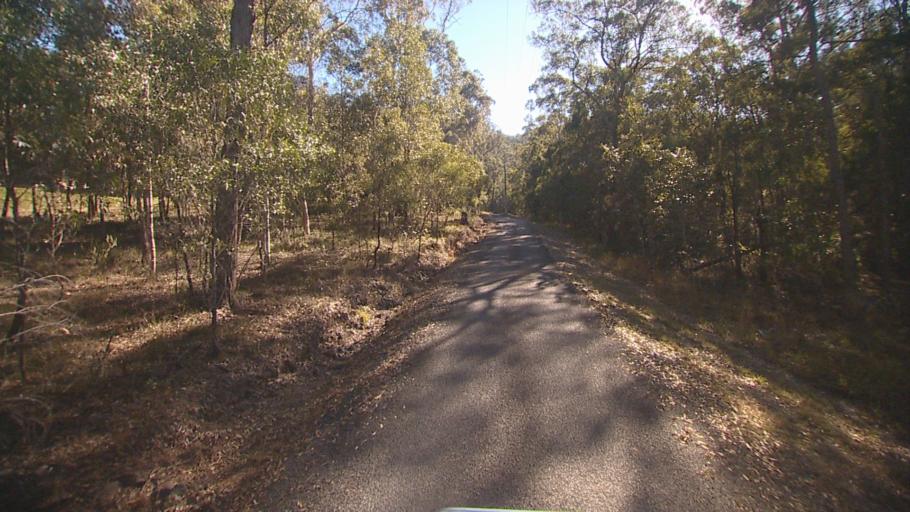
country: AU
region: Queensland
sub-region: Logan
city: Windaroo
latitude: -27.7894
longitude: 153.1714
